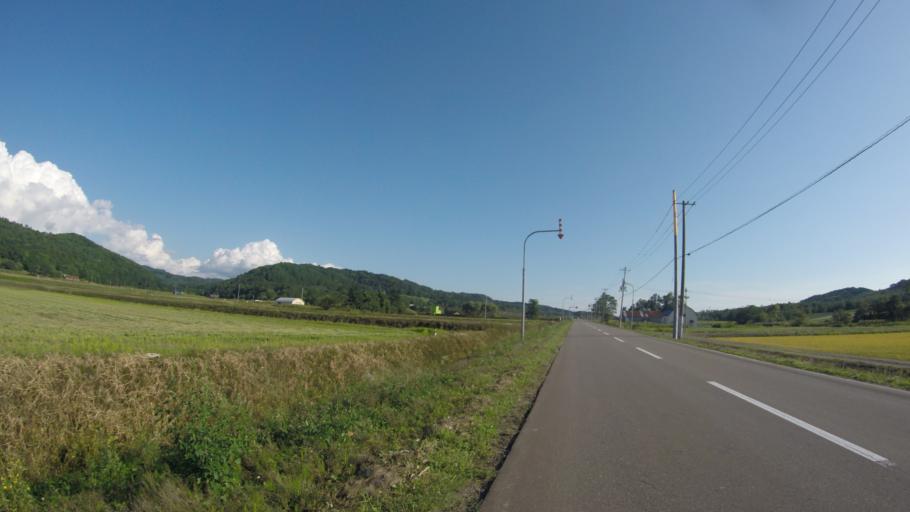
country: JP
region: Hokkaido
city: Iwamizawa
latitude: 43.1948
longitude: 141.8245
